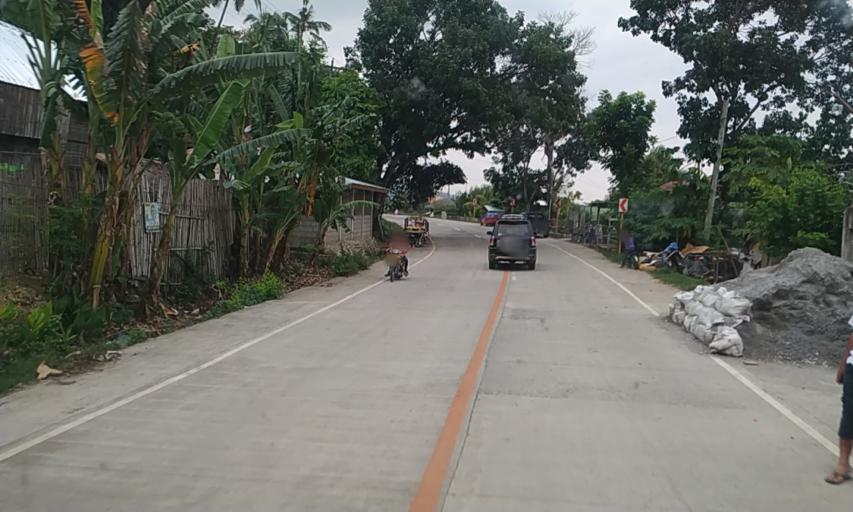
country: PH
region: Central Visayas
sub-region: Province of Negros Oriental
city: Basak
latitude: 10.2108
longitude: 123.3023
